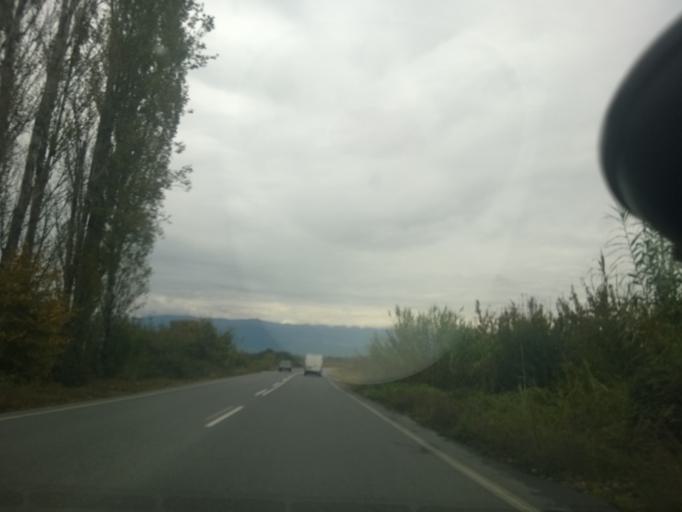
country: GR
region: Central Macedonia
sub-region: Nomos Pellis
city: Loutraki
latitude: 40.9724
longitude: 21.9726
